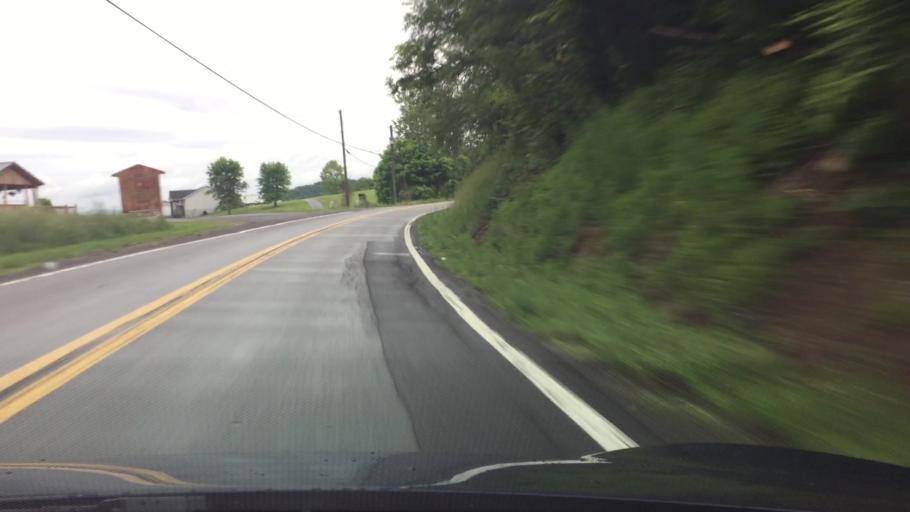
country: US
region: West Virginia
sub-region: Summers County
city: Hinton
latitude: 37.5662
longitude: -80.7912
